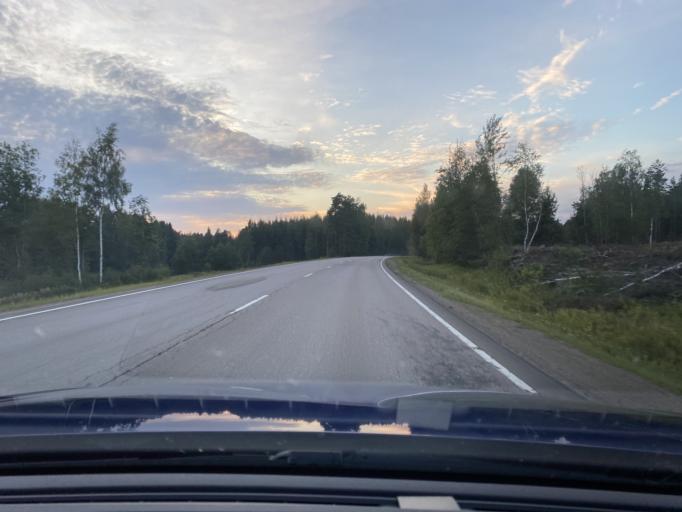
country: FI
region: Satakunta
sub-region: Pohjois-Satakunta
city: Honkajoki
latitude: 61.9421
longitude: 22.2342
